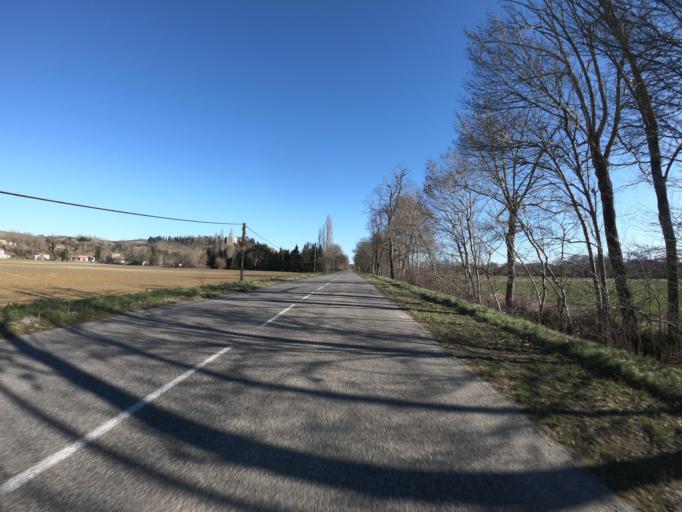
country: FR
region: Midi-Pyrenees
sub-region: Departement de l'Ariege
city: Mirepoix
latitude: 43.0966
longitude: 1.8716
